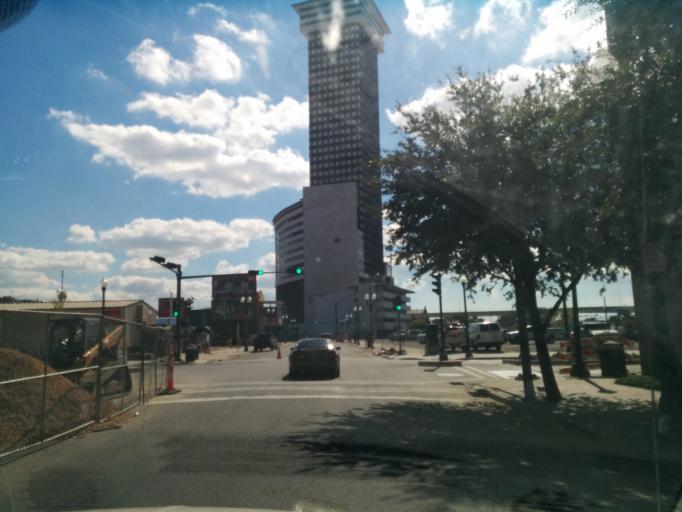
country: US
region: Louisiana
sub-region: Orleans Parish
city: New Orleans
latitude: 29.9488
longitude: -90.0755
